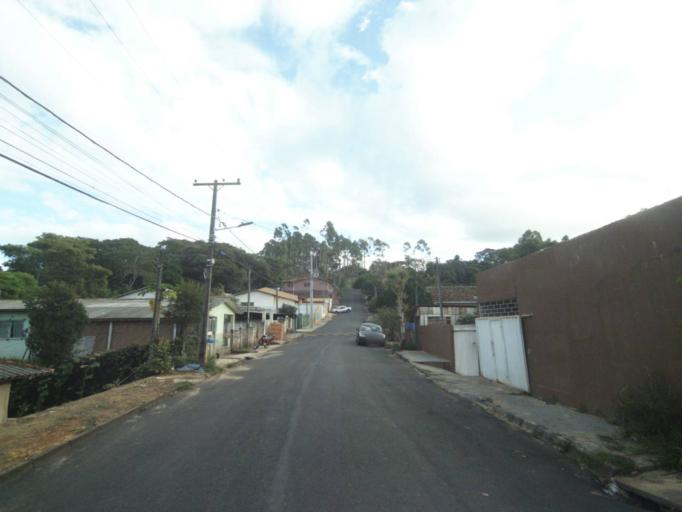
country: BR
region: Parana
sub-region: Telemaco Borba
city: Telemaco Borba
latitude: -24.3279
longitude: -50.6080
